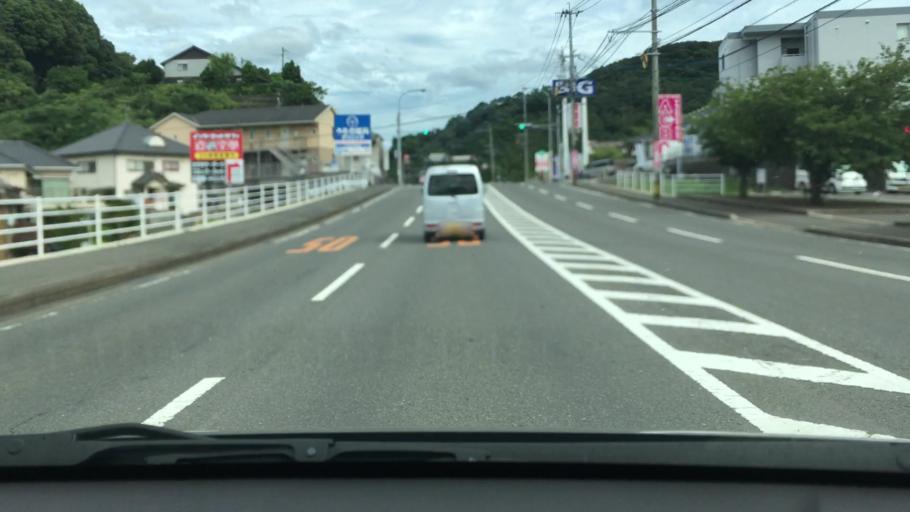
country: JP
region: Nagasaki
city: Togitsu
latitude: 32.8356
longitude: 129.8389
